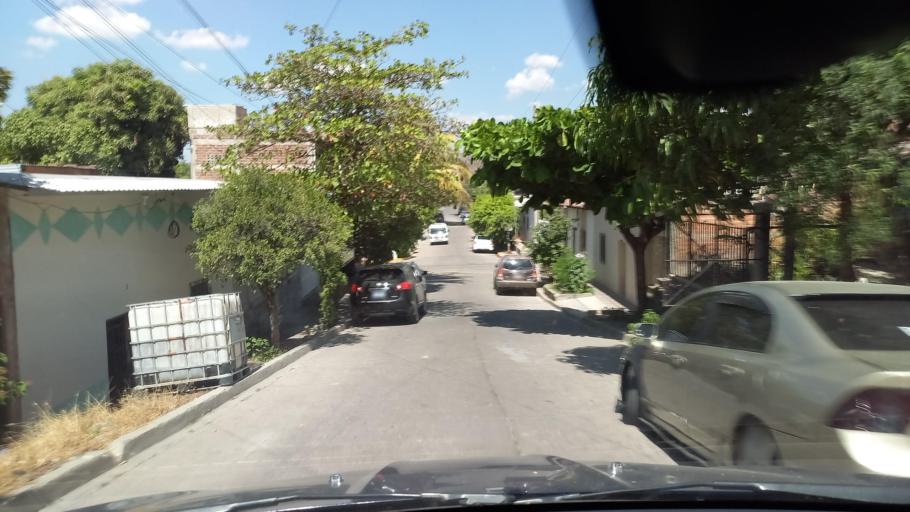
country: SV
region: Santa Ana
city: Metapan
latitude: 14.3341
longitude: -89.4458
